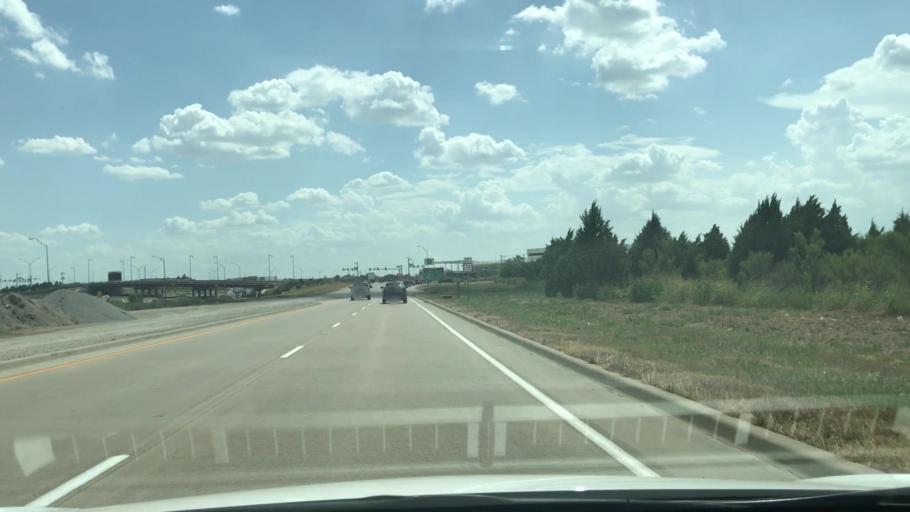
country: US
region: Texas
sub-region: Tarrant County
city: Grapevine
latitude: 32.9263
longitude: -97.0574
